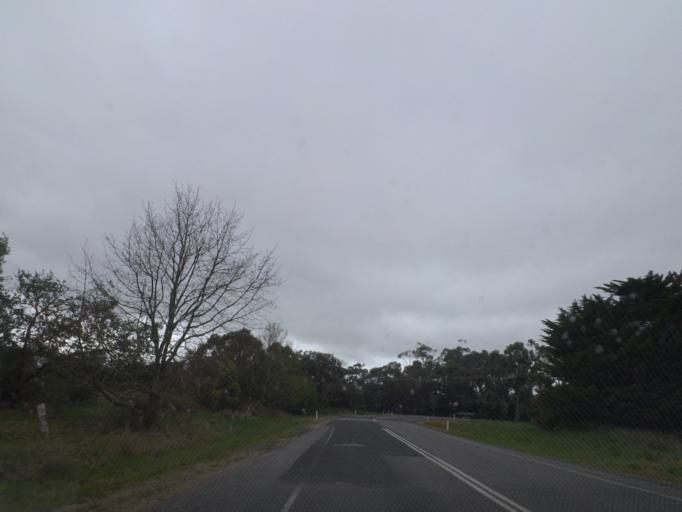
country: AU
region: Victoria
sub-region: Hume
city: Sunbury
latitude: -37.3266
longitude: 144.5868
